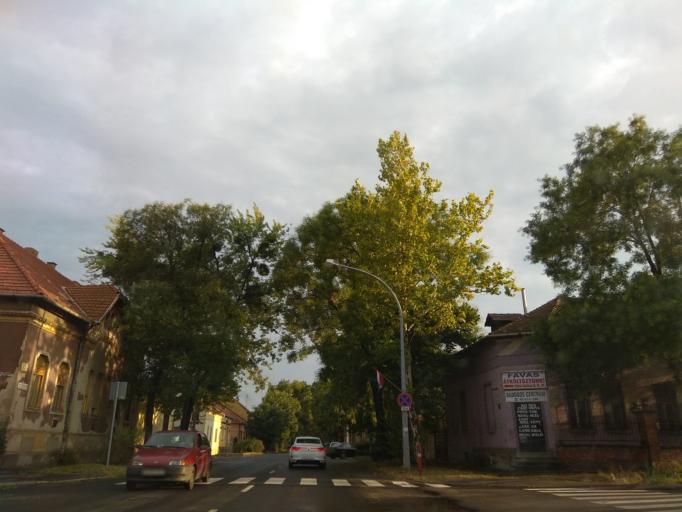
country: HU
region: Borsod-Abauj-Zemplen
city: Miskolc
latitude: 48.0936
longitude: 20.7961
